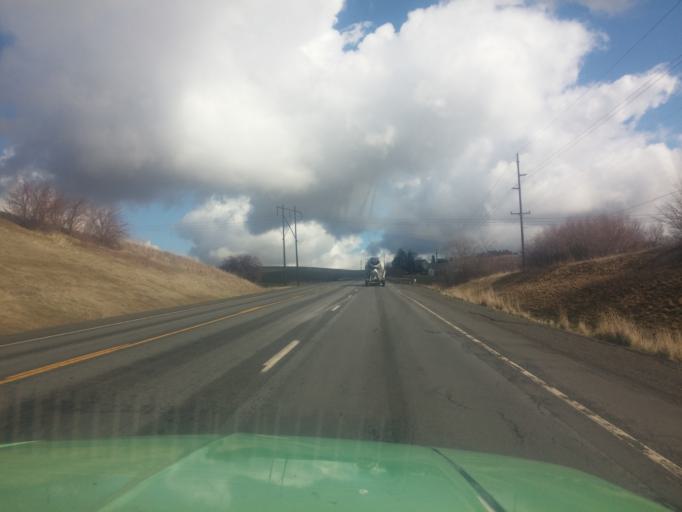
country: US
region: Idaho
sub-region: Latah County
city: Moscow
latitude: 46.8605
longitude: -117.0172
